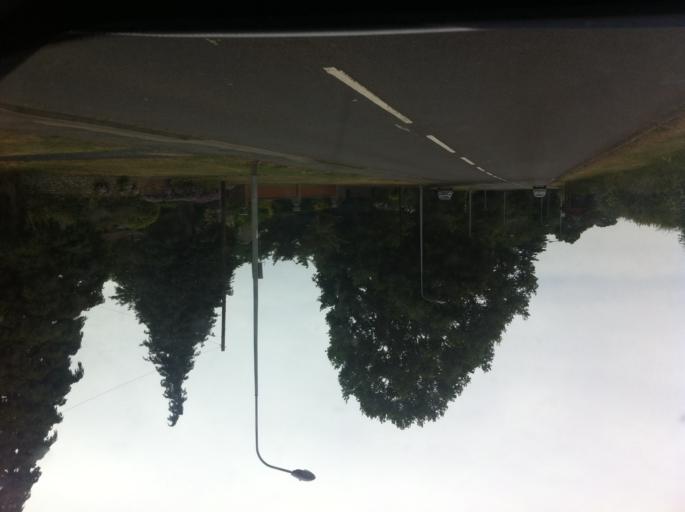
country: GB
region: England
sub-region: Northamptonshire
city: Earls Barton
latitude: 52.2692
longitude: -0.7574
